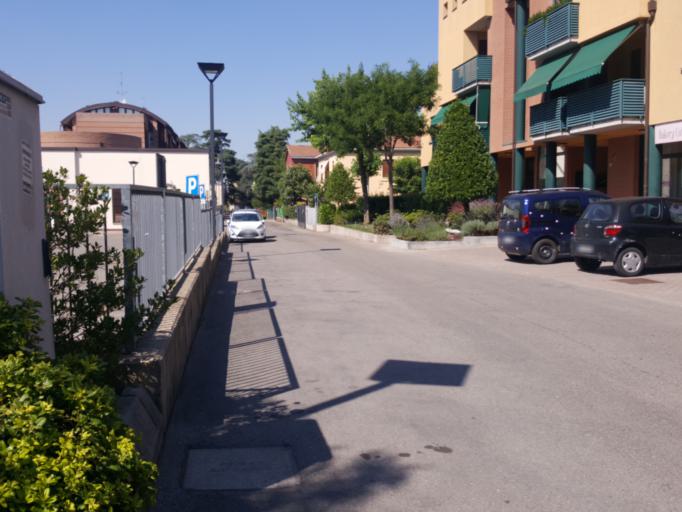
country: IT
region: Emilia-Romagna
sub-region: Provincia di Bologna
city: Castel San Pietro Terme
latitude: 44.4002
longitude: 11.5883
